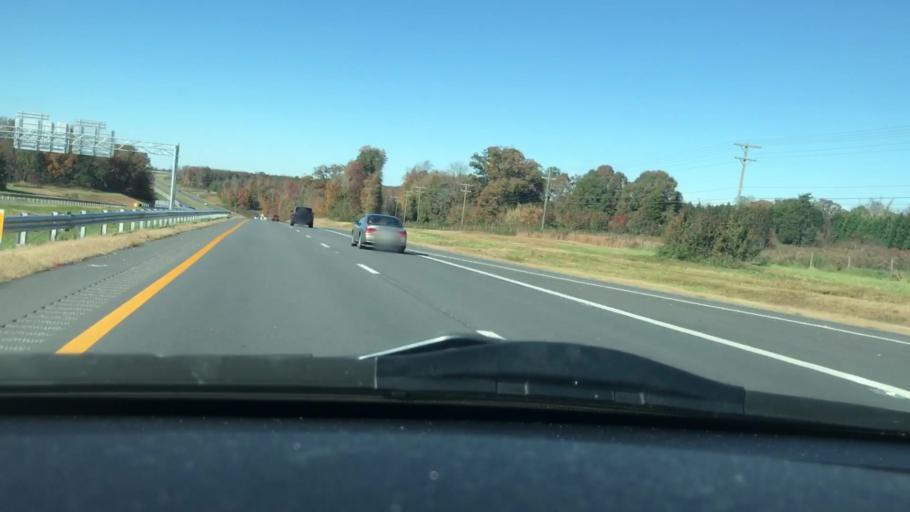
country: US
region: North Carolina
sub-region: Guilford County
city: Summerfield
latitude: 36.2499
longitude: -79.9219
